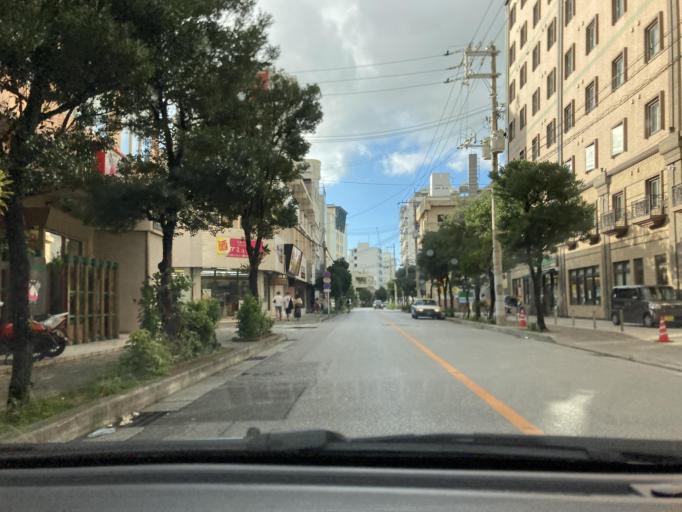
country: JP
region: Okinawa
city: Naha-shi
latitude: 26.2194
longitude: 127.6794
